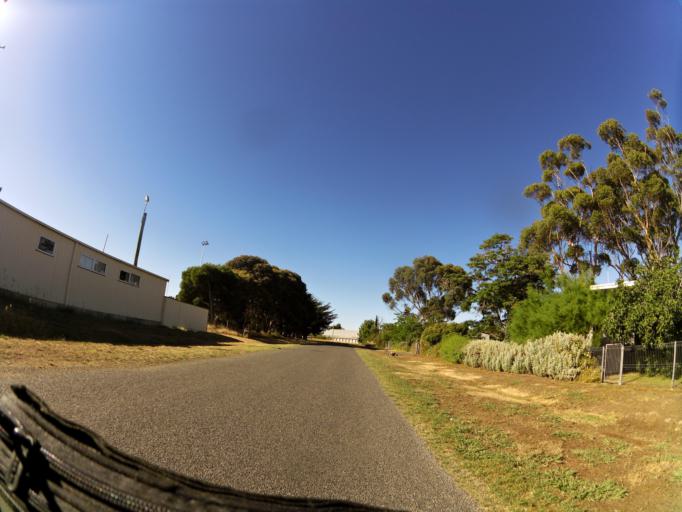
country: AU
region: Victoria
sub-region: Ballarat North
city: Delacombe
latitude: -37.6887
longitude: 143.3645
